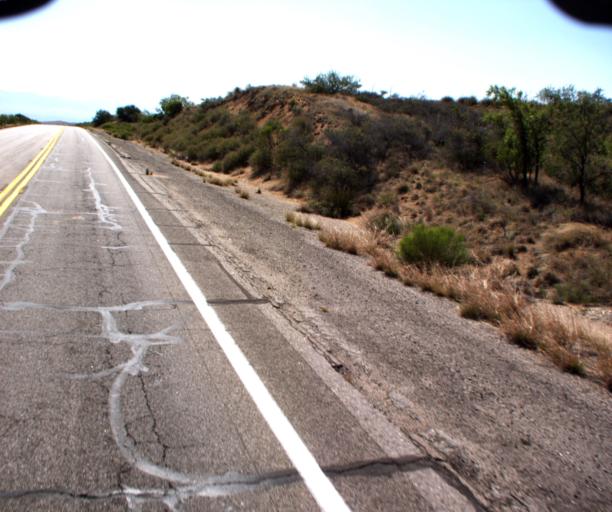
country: US
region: Arizona
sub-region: Pinal County
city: Oracle
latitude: 32.6236
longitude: -110.7600
